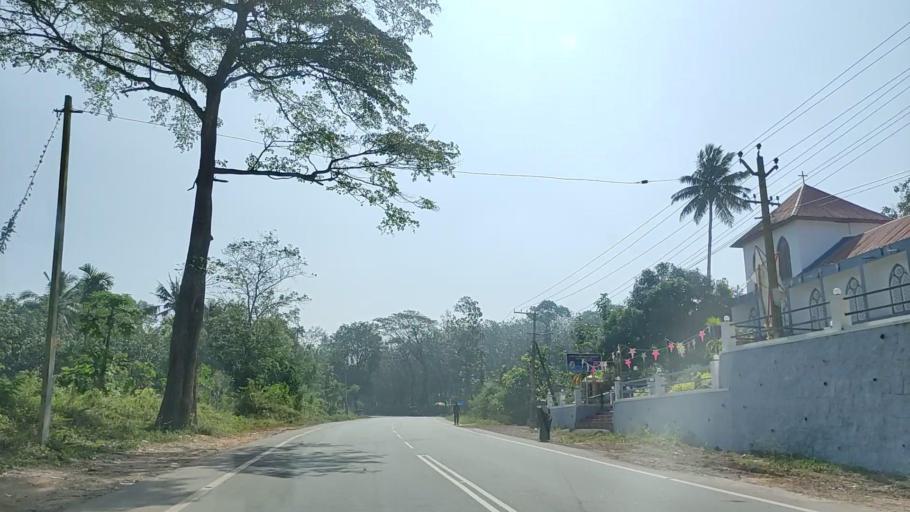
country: IN
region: Kerala
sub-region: Kollam
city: Punalur
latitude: 8.9301
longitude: 76.9706
